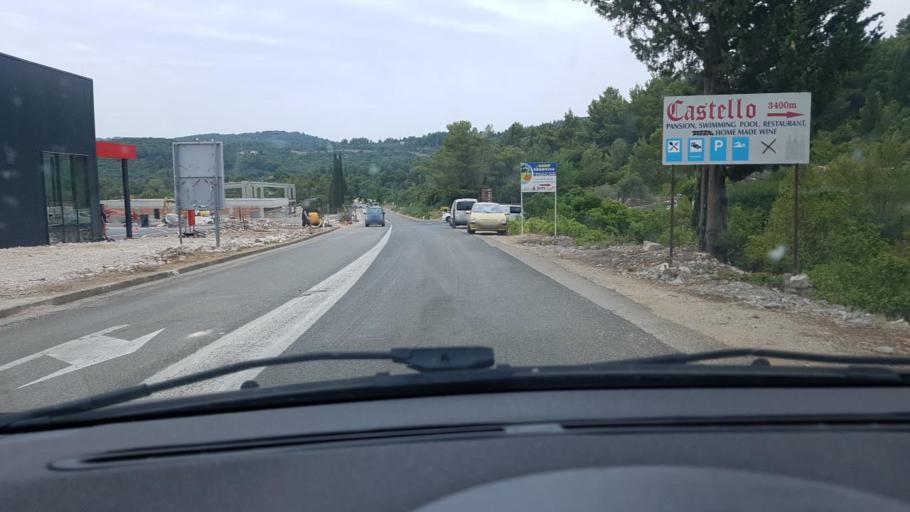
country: HR
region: Dubrovacko-Neretvanska
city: Korcula
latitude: 42.9542
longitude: 17.1274
